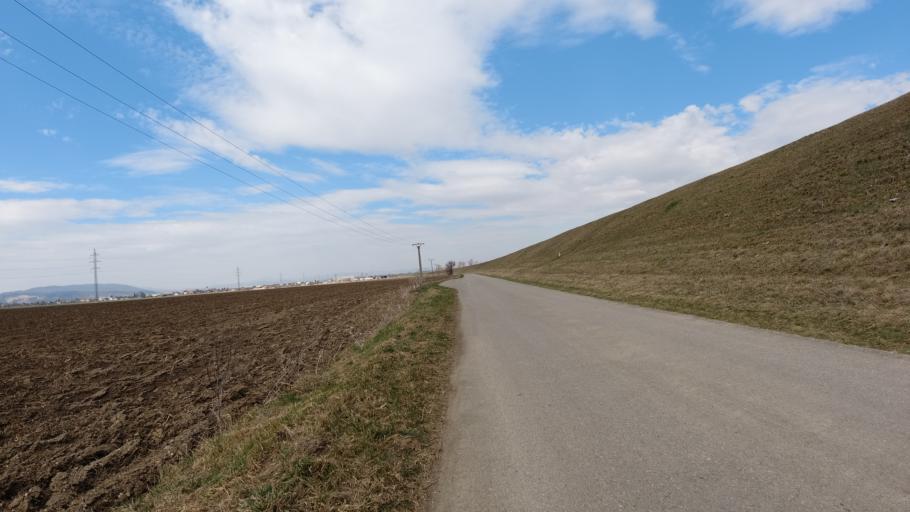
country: SK
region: Nitriansky
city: Cachtice
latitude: 48.6762
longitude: 17.8613
